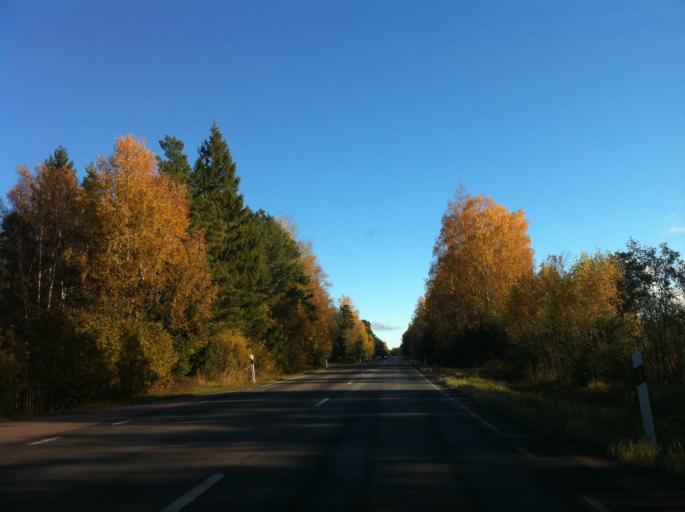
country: SE
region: Uppsala
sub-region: Osthammars Kommun
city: Oregrund
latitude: 60.3301
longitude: 18.3921
